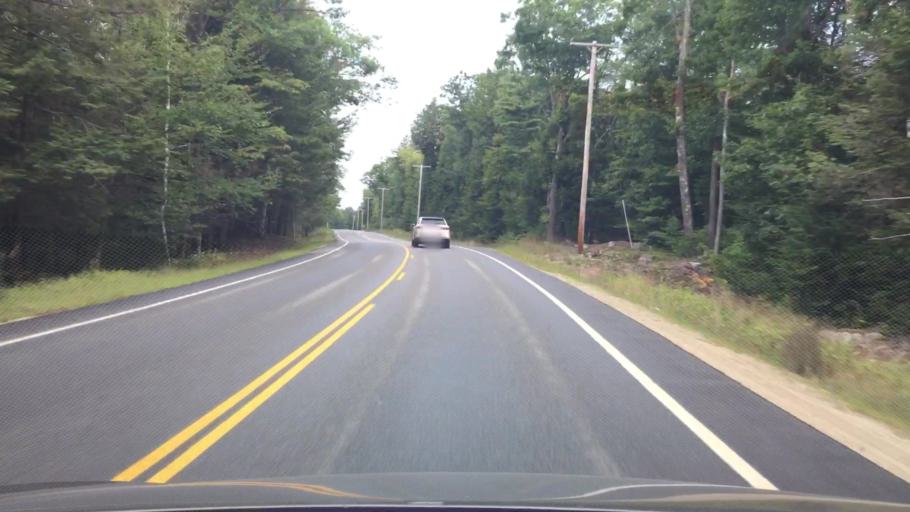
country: US
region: Maine
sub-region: Oxford County
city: Hartford
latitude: 44.3609
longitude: -70.3108
